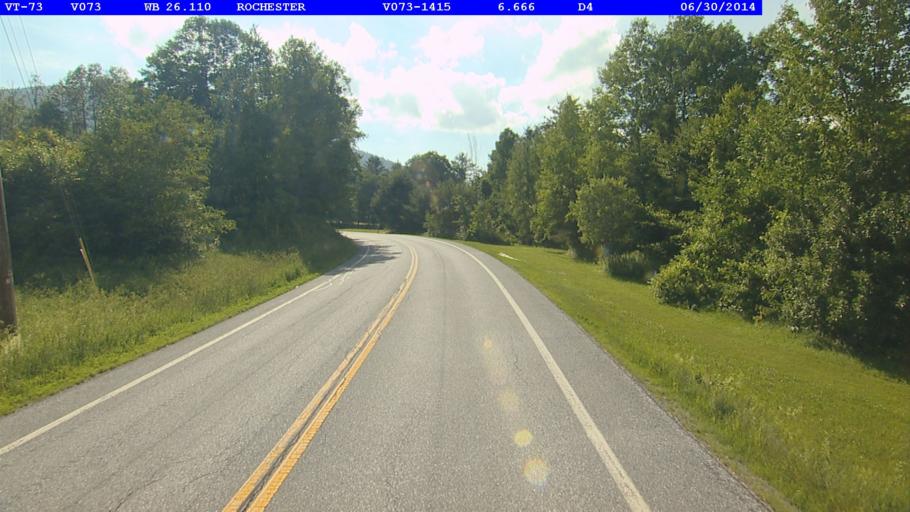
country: US
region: Vermont
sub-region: Orange County
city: Randolph
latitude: 43.8492
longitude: -72.8436
